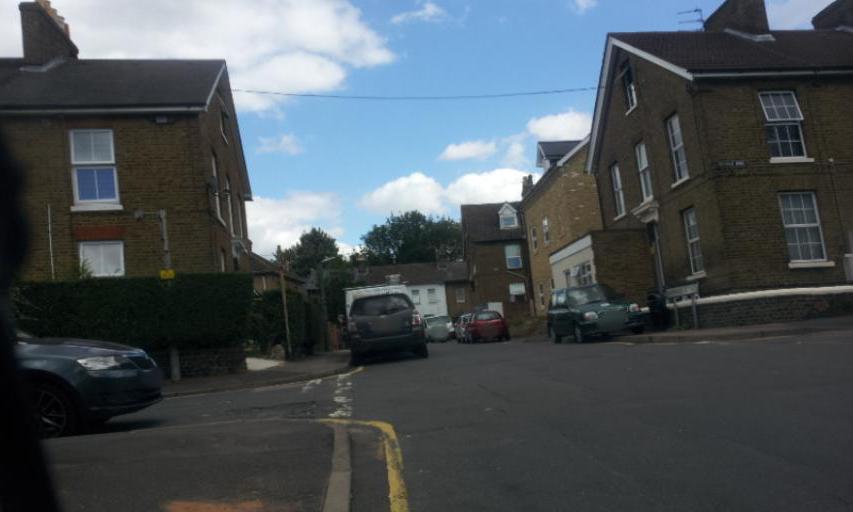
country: GB
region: England
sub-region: Kent
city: Maidstone
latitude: 51.2694
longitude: 0.5271
